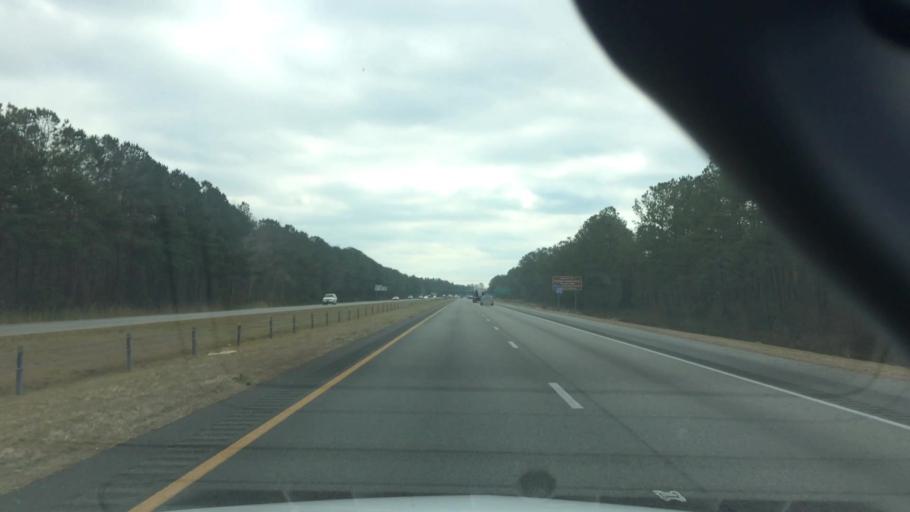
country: US
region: North Carolina
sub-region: New Hanover County
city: Skippers Corner
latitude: 34.3363
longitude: -77.8773
